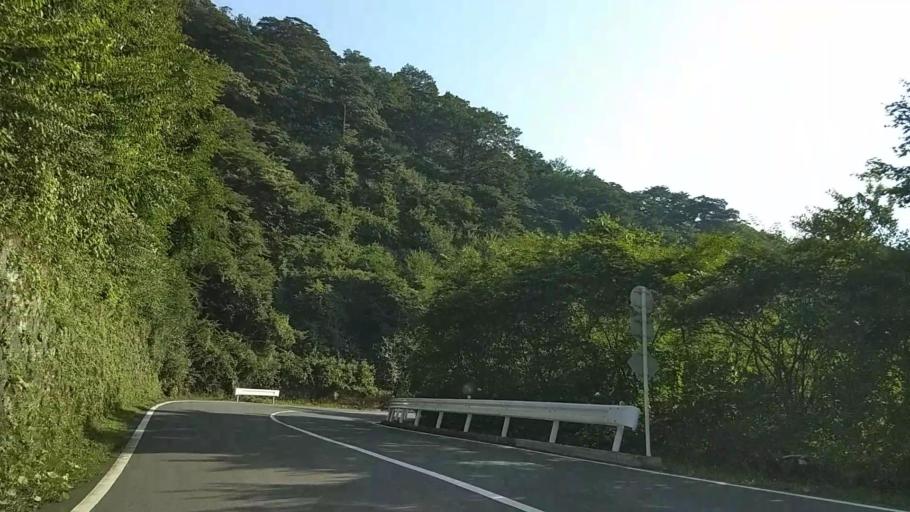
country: JP
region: Kanagawa
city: Hakone
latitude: 35.2184
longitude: 138.9809
